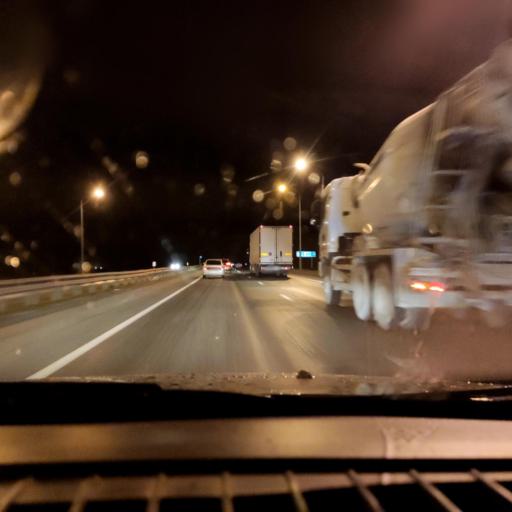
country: RU
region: Samara
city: Zhigulevsk
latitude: 53.5436
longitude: 49.5132
